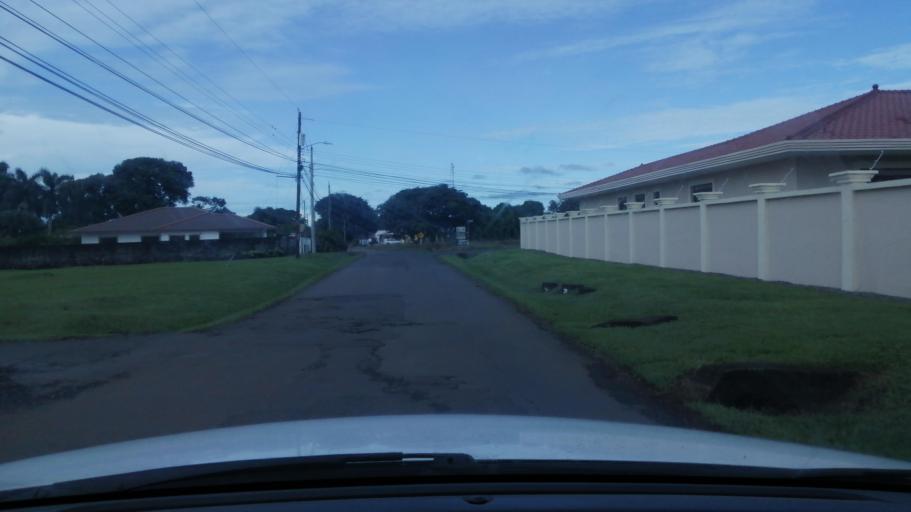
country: PA
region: Chiriqui
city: El Quiteno
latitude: 8.4607
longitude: -82.4175
